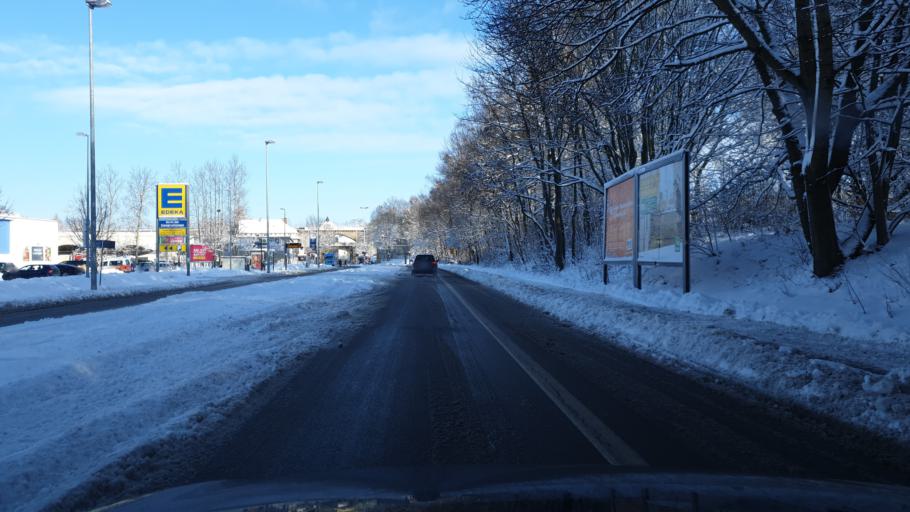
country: DE
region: Saxony
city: Chemnitz
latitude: 50.8510
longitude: 12.9291
